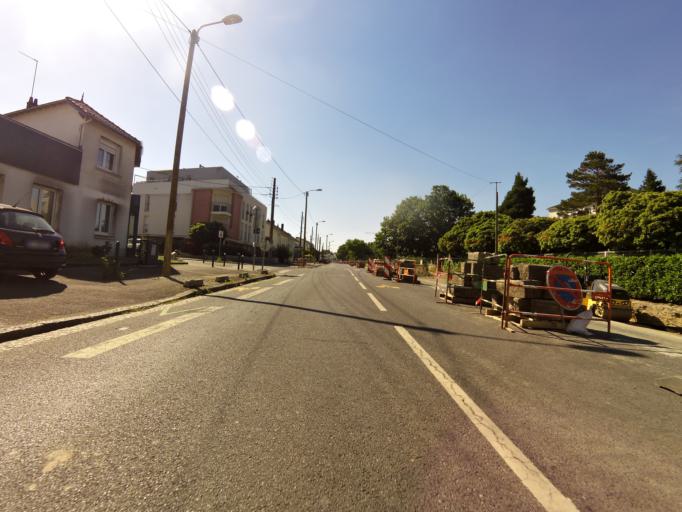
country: FR
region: Pays de la Loire
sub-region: Departement de la Loire-Atlantique
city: Nantes
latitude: 47.2513
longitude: -1.5714
